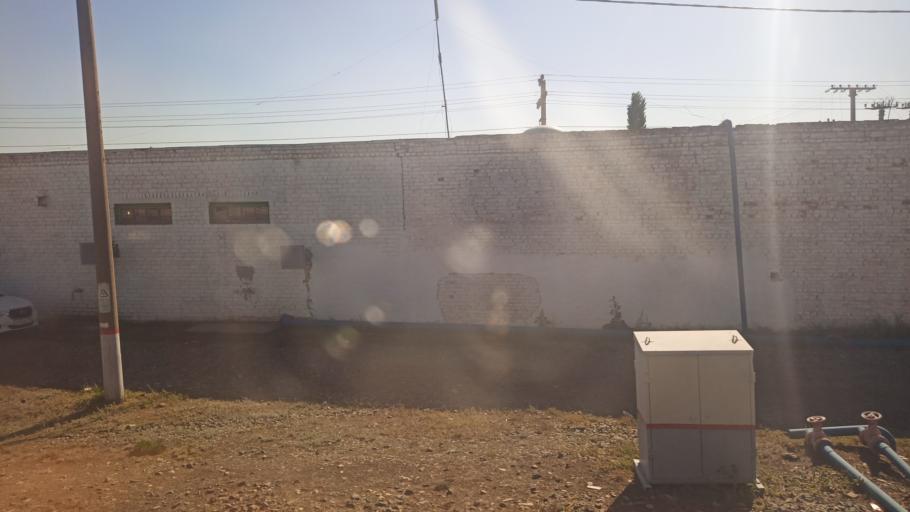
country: RU
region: Saratov
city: Pushkino
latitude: 51.2351
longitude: 46.9815
